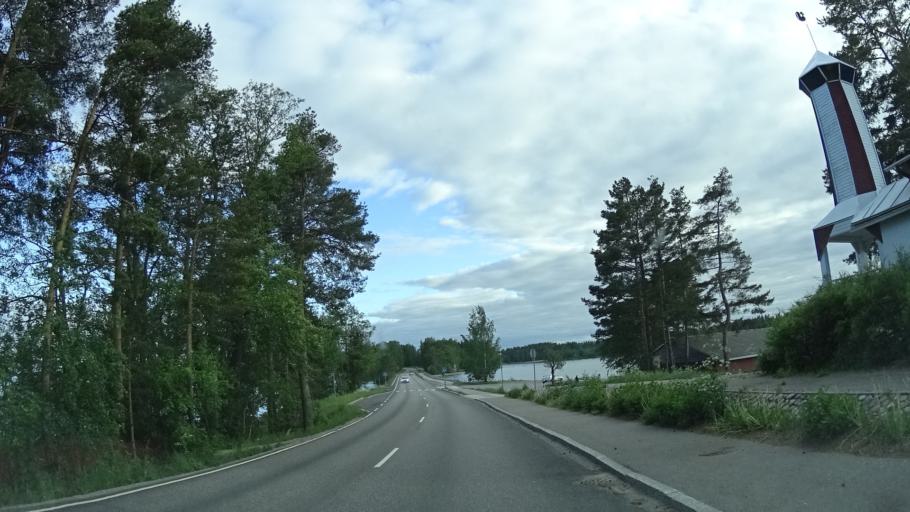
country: FI
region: Paijanne Tavastia
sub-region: Lahti
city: Asikkala
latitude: 61.2677
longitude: 25.5219
